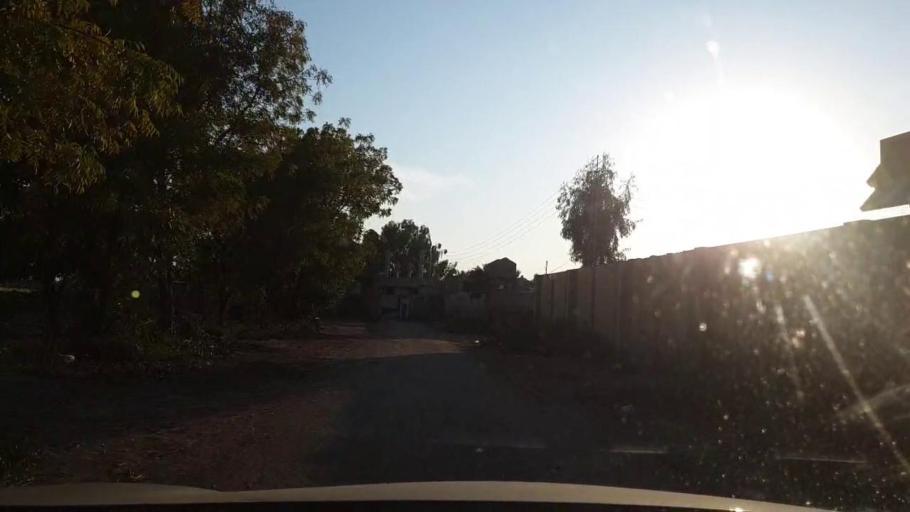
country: PK
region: Sindh
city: Tando Adam
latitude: 25.6137
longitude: 68.6779
